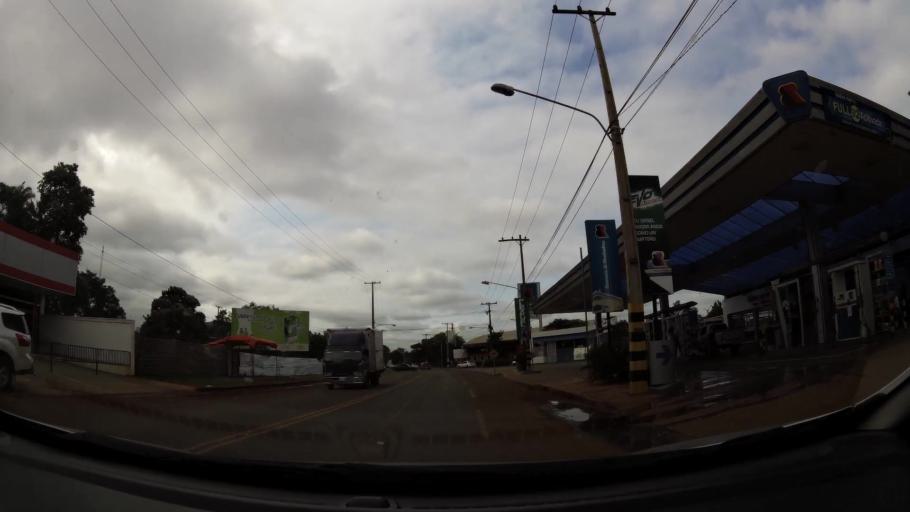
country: PY
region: Alto Parana
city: Ciudad del Este
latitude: -25.4059
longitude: -54.6297
